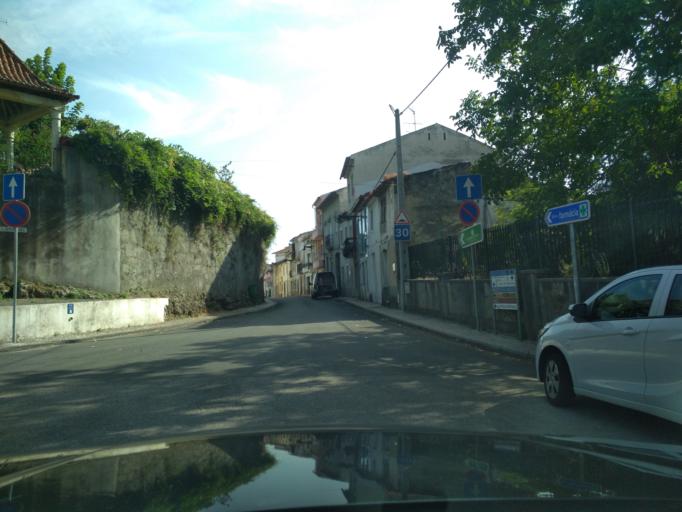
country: PT
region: Coimbra
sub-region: Condeixa-A-Nova
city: Condeixa-a-Nova
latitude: 40.1397
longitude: -8.4685
